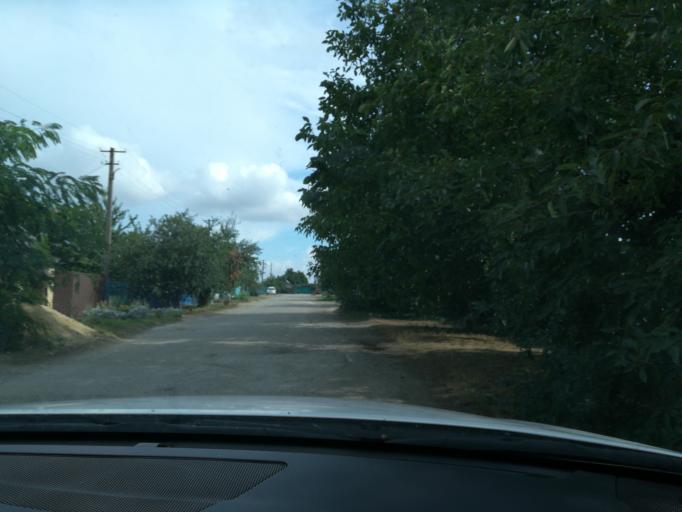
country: RU
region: Krasnodarskiy
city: Strelka
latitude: 45.1726
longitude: 37.2691
